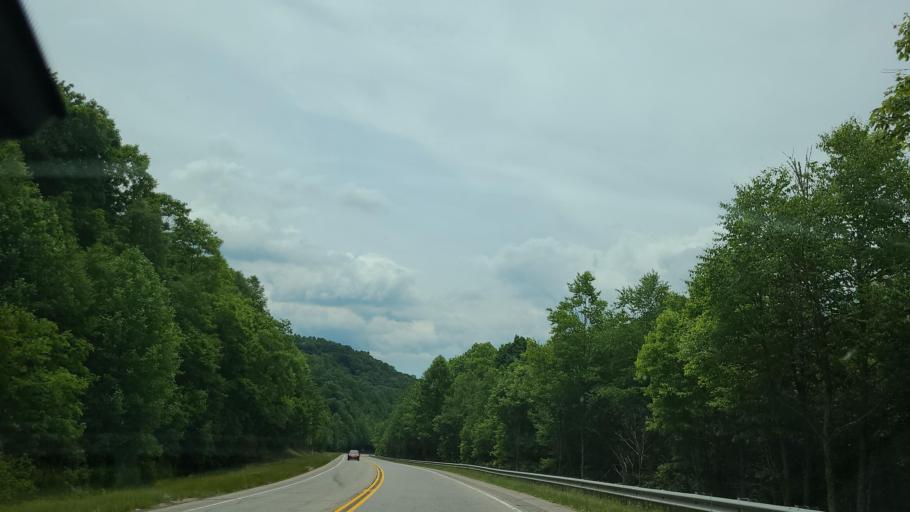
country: US
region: North Carolina
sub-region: Macon County
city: Franklin
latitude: 35.1170
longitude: -83.5512
